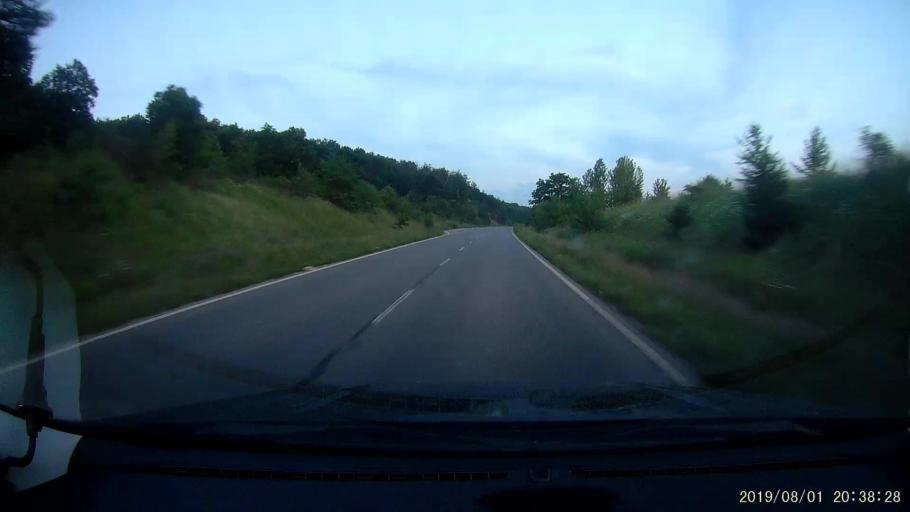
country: BG
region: Yambol
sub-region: Obshtina Elkhovo
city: Elkhovo
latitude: 42.0257
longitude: 26.6016
